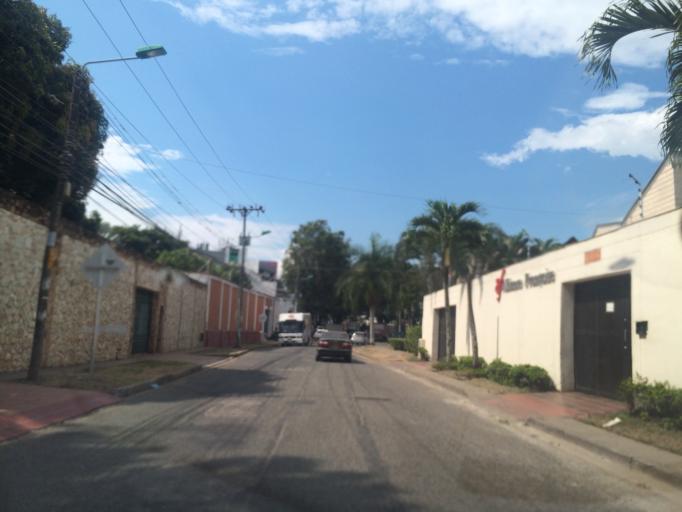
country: CO
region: Valle del Cauca
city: Cali
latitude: 3.3610
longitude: -76.5319
